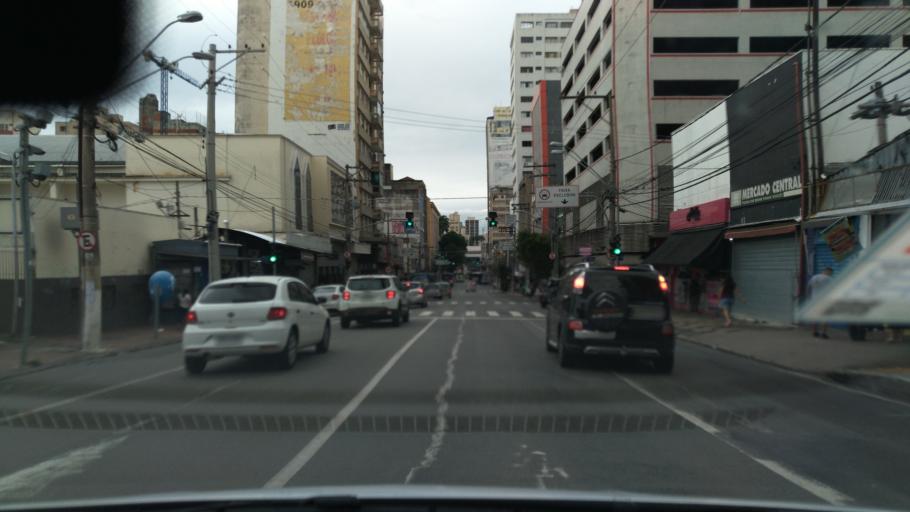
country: BR
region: Sao Paulo
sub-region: Campinas
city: Campinas
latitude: -22.9059
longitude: -47.0633
